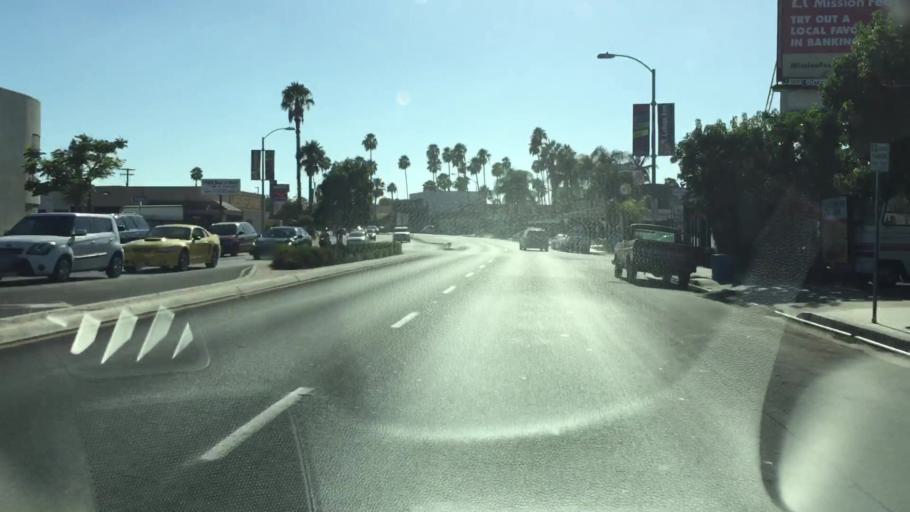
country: US
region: California
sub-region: San Diego County
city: La Mesa
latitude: 32.7669
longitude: -117.0579
